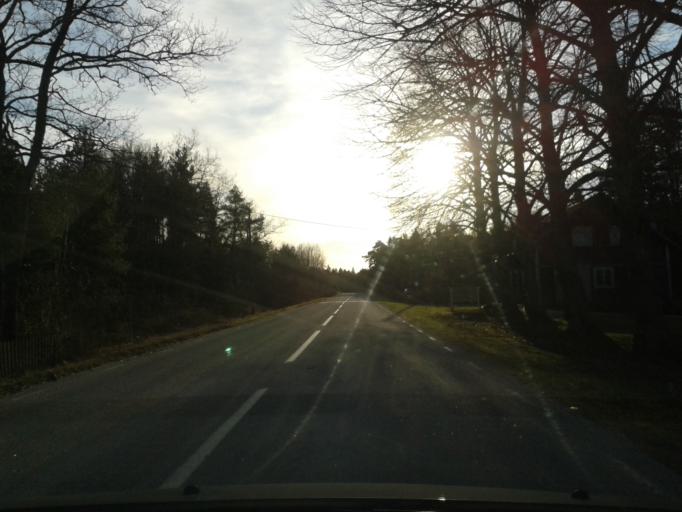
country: SE
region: Gotland
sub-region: Gotland
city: Hemse
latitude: 57.3593
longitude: 18.6855
